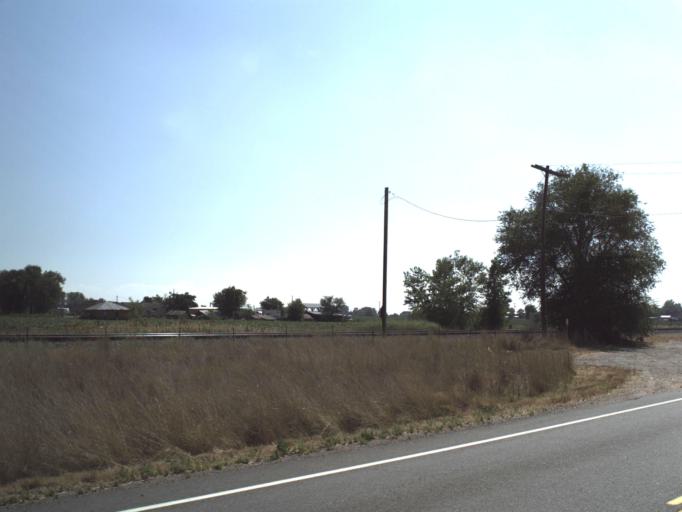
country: US
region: Utah
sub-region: Weber County
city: West Haven
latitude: 41.2444
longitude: -112.0743
